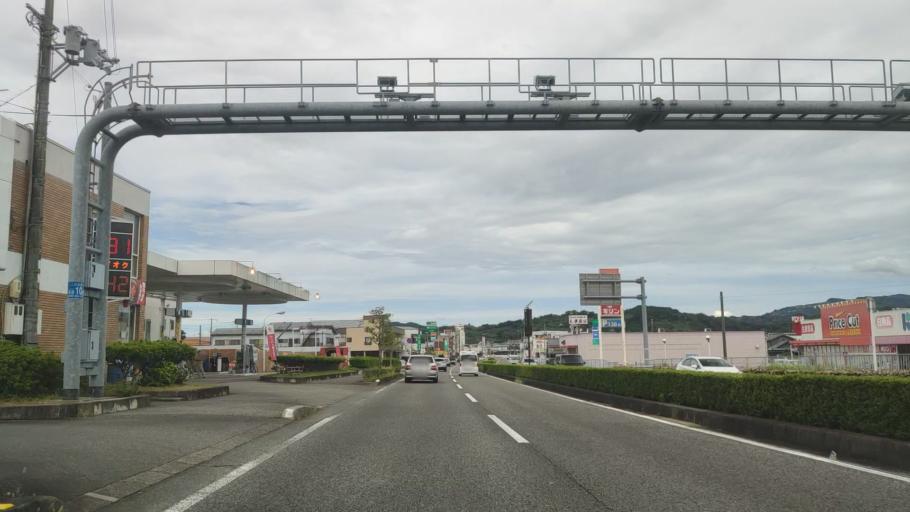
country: JP
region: Wakayama
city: Tanabe
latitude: 33.7381
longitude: 135.3957
